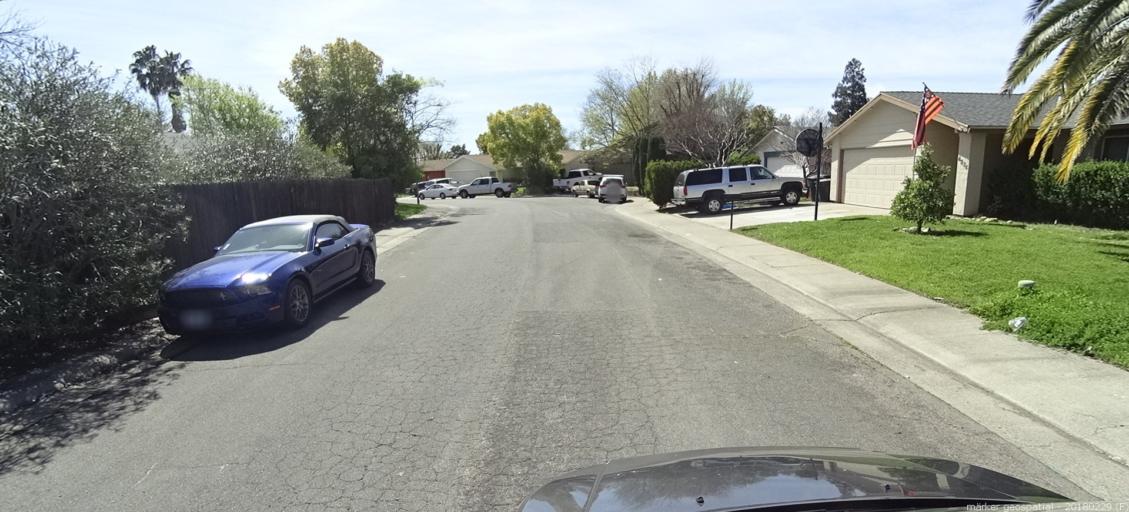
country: US
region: California
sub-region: Sacramento County
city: Rosemont
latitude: 38.5418
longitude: -121.3480
